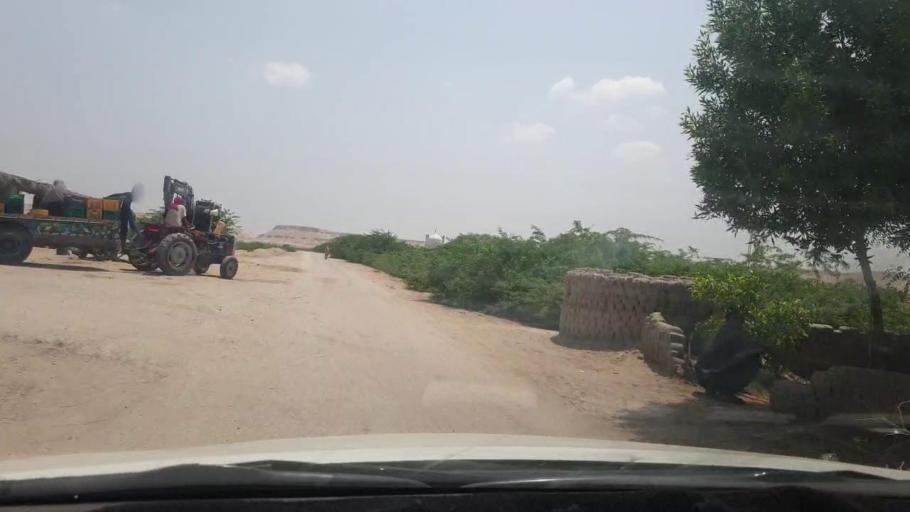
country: PK
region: Sindh
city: Khairpur
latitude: 27.5296
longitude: 68.9020
